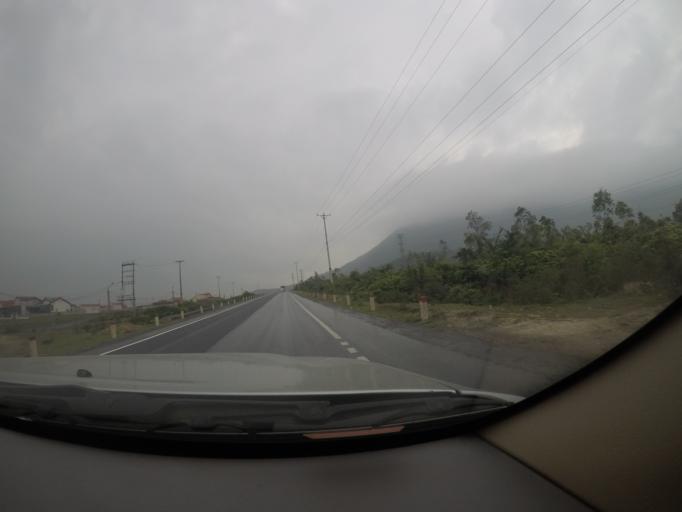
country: VN
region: Ha Tinh
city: Ky Anh
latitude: 17.9987
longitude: 106.4509
